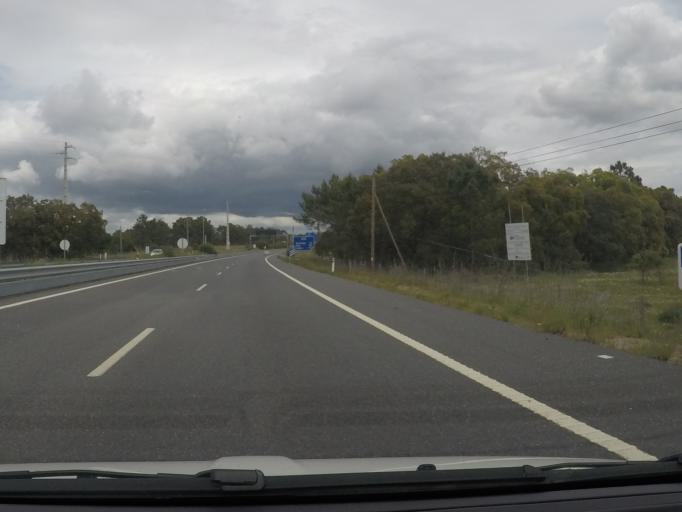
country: PT
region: Setubal
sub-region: Sines
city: Sines
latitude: 37.9720
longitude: -8.8229
